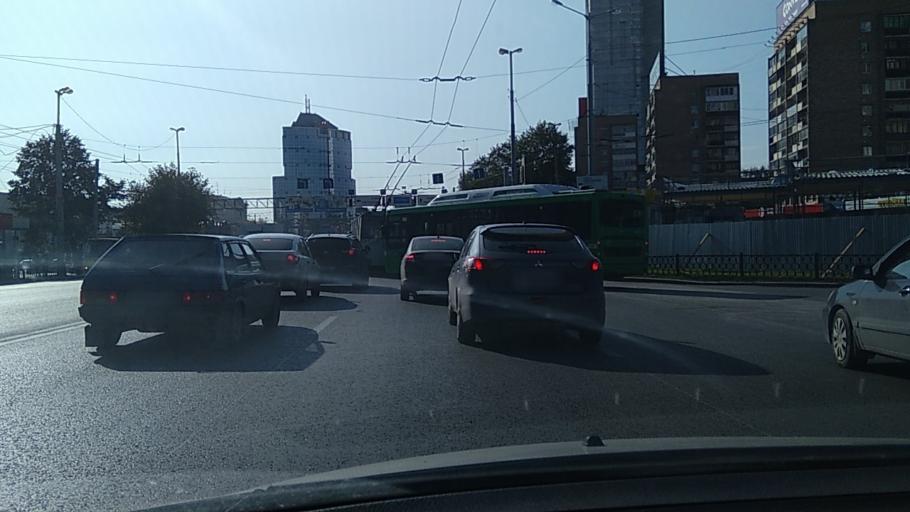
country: RU
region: Sverdlovsk
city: Yekaterinburg
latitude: 56.8567
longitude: 60.6059
